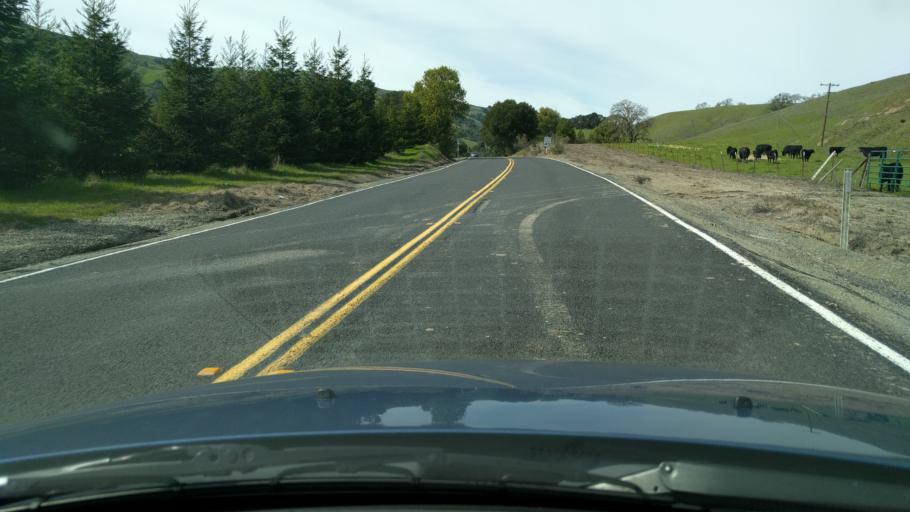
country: US
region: California
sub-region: Contra Costa County
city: Danville
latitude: 37.7950
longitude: -122.0190
